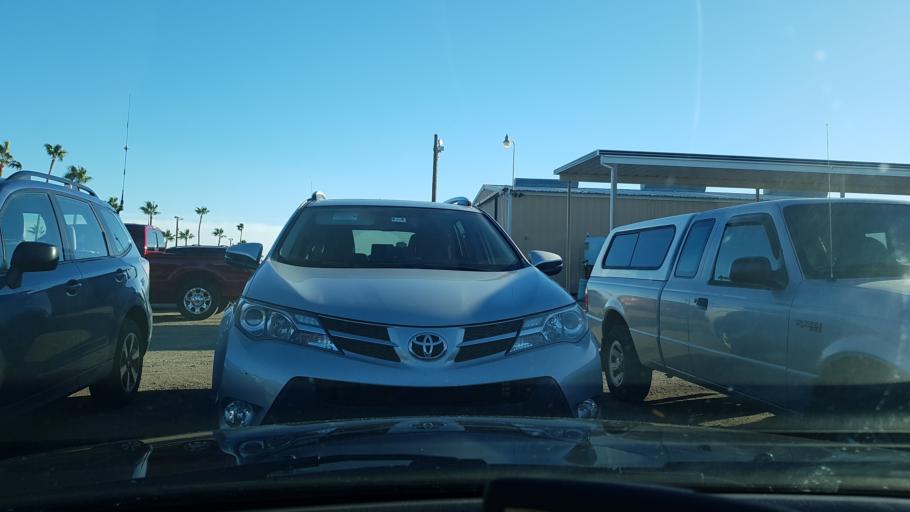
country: US
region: Arizona
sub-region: Yuma County
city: Yuma
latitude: 32.6722
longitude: -114.5929
